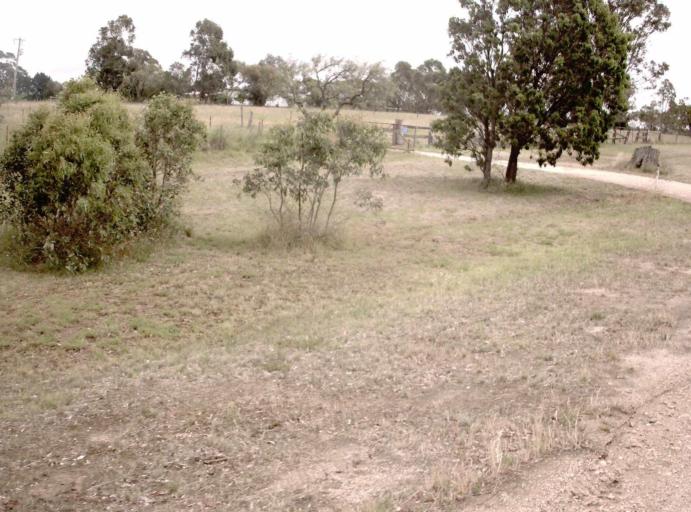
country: AU
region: Victoria
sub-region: Wellington
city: Sale
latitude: -37.9460
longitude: 147.0902
